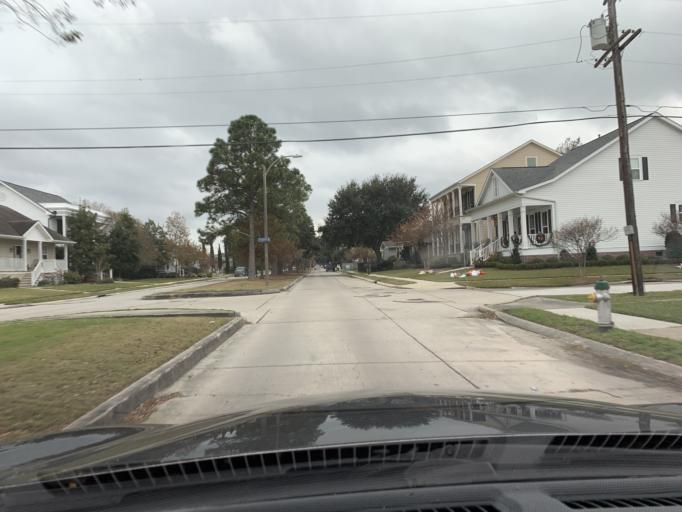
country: US
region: Louisiana
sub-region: Jefferson Parish
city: Metairie
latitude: 30.0138
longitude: -90.1017
